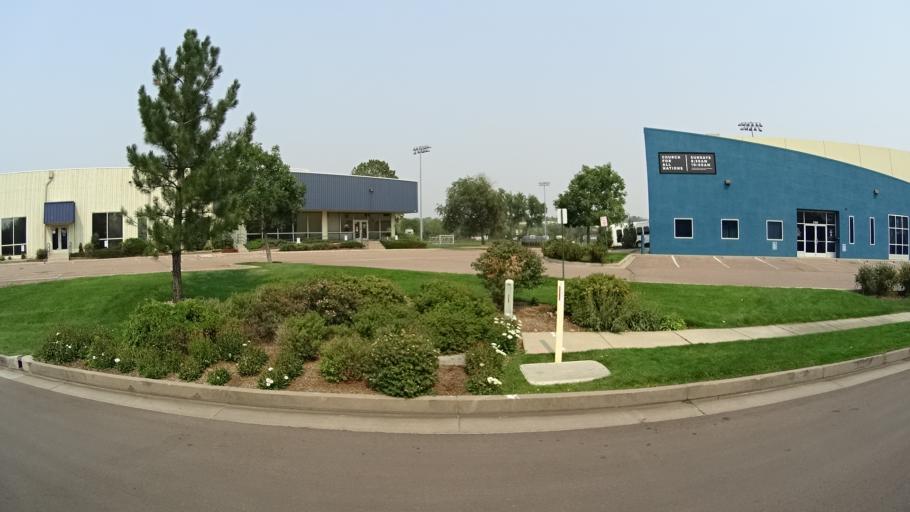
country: US
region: Colorado
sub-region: El Paso County
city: Stratmoor
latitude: 38.7918
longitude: -104.7865
